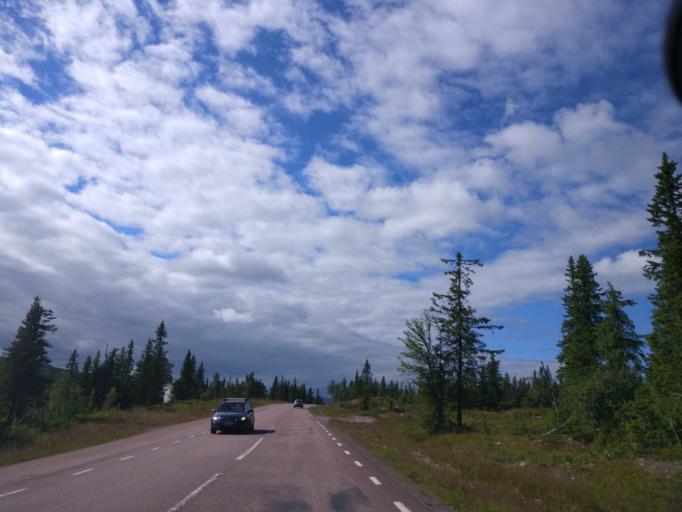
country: SE
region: Dalarna
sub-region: Malung-Saelens kommun
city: Malung
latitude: 61.1625
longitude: 13.1077
